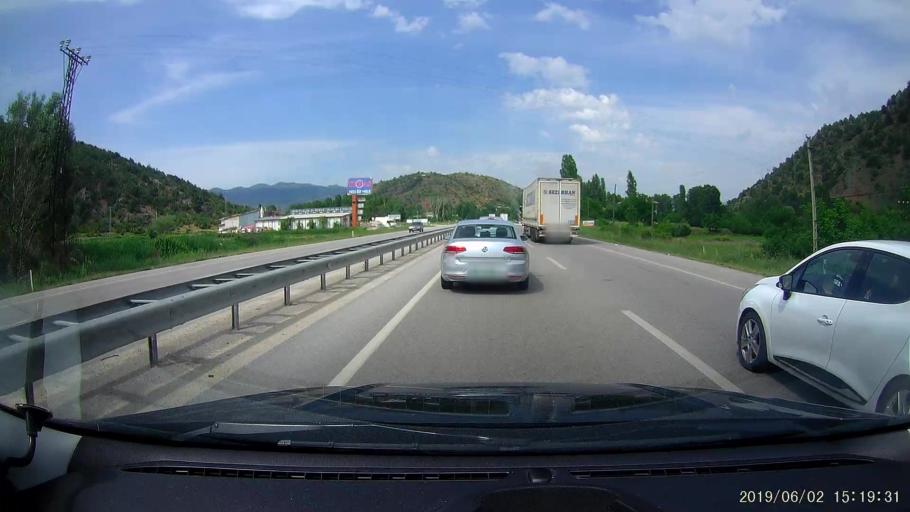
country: TR
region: Corum
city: Osmancik
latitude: 40.9720
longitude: 34.9103
